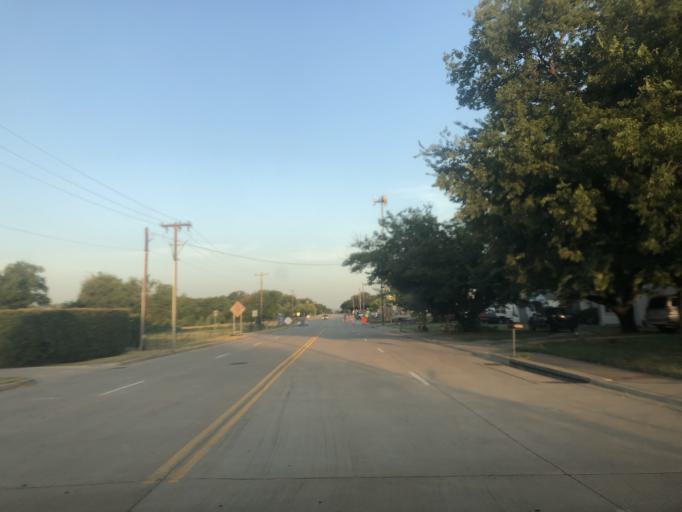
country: US
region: Texas
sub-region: Tarrant County
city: Lake Worth
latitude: 32.8105
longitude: -97.4348
